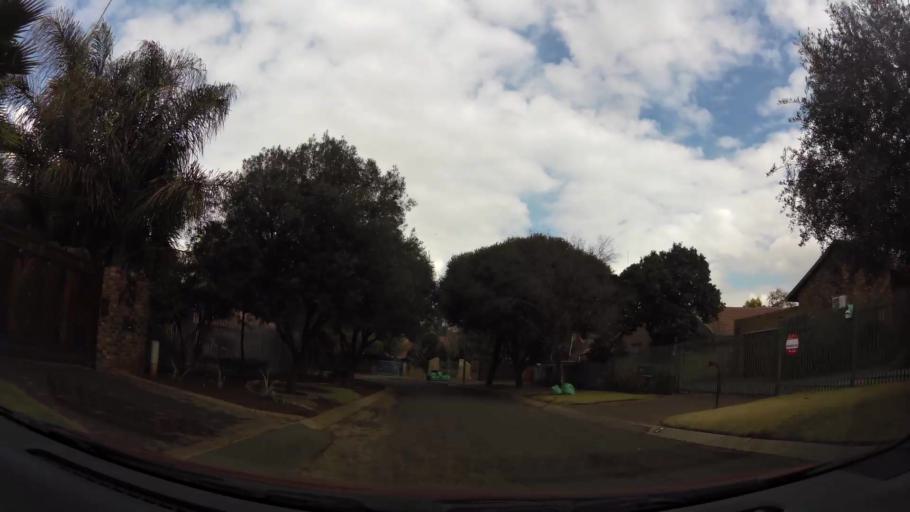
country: ZA
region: Gauteng
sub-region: Sedibeng District Municipality
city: Vanderbijlpark
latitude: -26.7415
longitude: 27.8499
